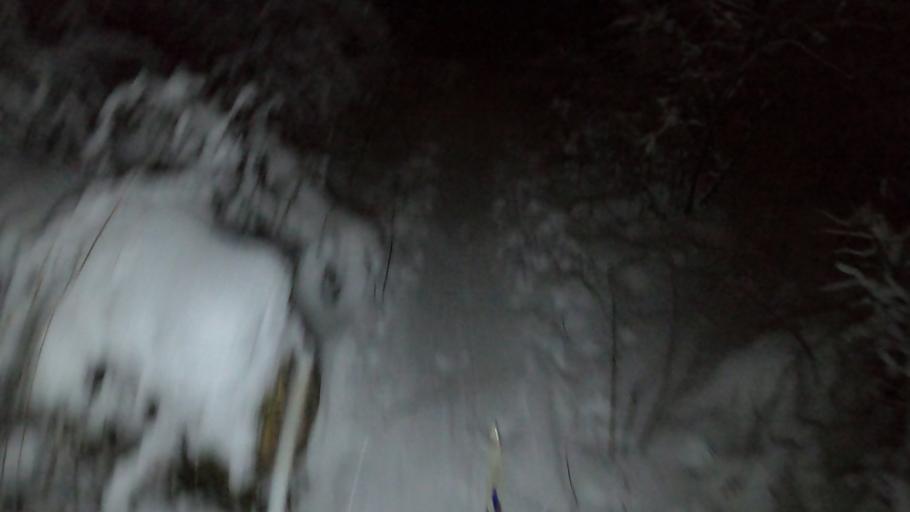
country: RU
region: Moskovskaya
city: Opalikha
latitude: 55.8617
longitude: 37.2335
